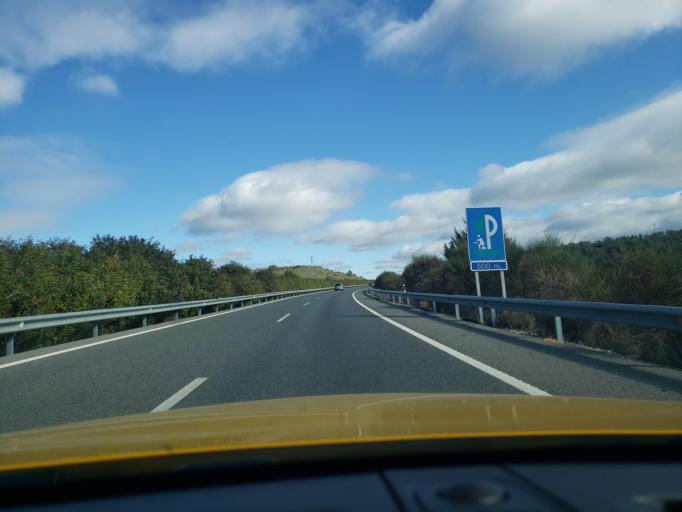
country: ES
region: Andalusia
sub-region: Provincia de Malaga
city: Villanueva del Rosario
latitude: 37.0399
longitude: -4.3863
